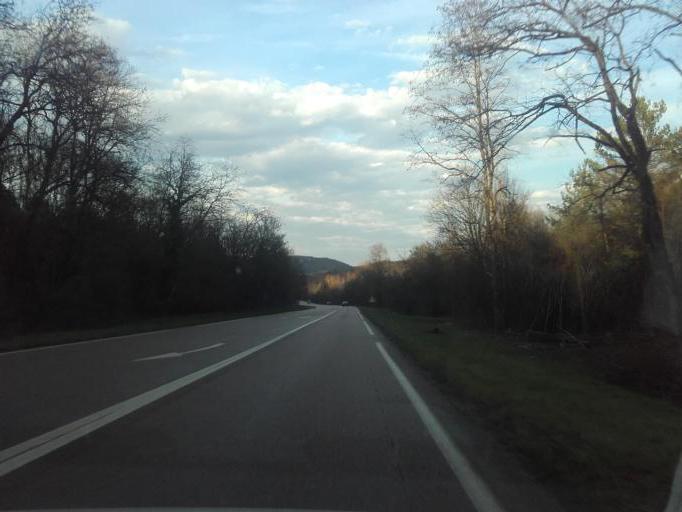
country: FR
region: Bourgogne
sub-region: Departement de la Cote-d'Or
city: Corpeau
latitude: 46.9409
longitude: 4.6974
